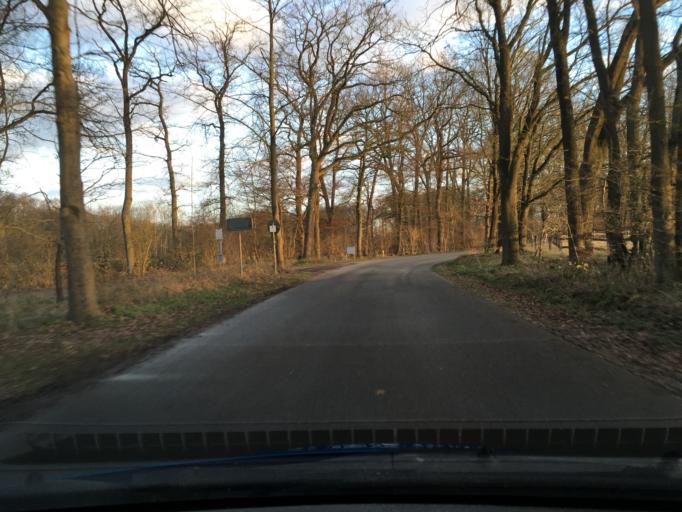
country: DE
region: Lower Saxony
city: Oldendorf
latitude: 53.1411
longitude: 10.2018
